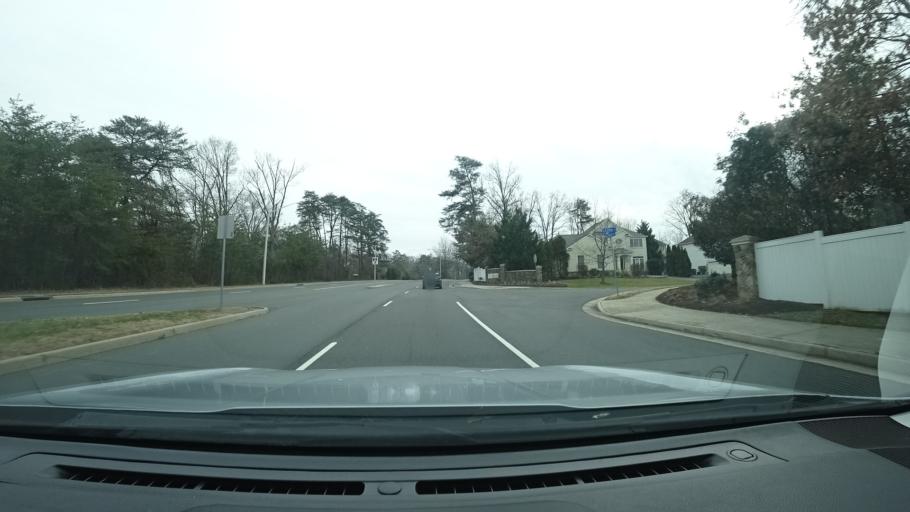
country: US
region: Virginia
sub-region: Fairfax County
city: Herndon
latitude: 38.9740
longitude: -77.3704
